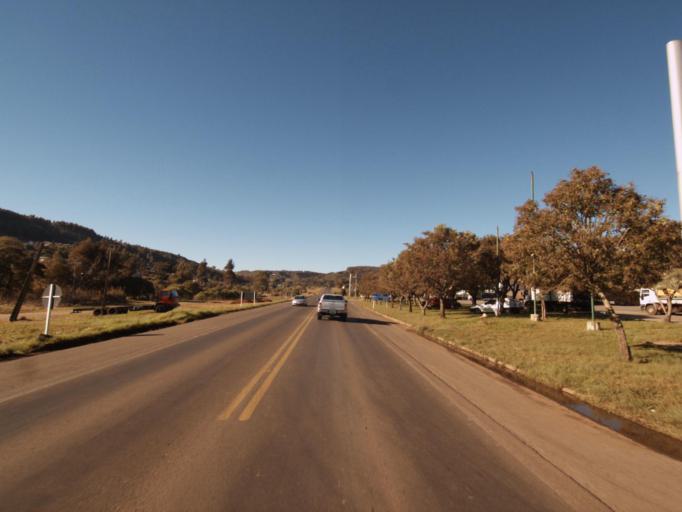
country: BR
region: Santa Catarina
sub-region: Concordia
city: Concordia
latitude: -26.8757
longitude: -52.0166
